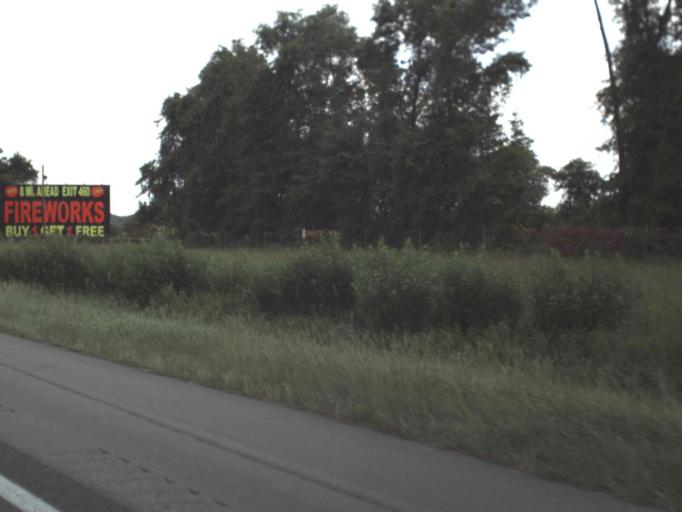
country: US
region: Georgia
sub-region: Echols County
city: Statenville
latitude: 30.6067
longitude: -83.1328
